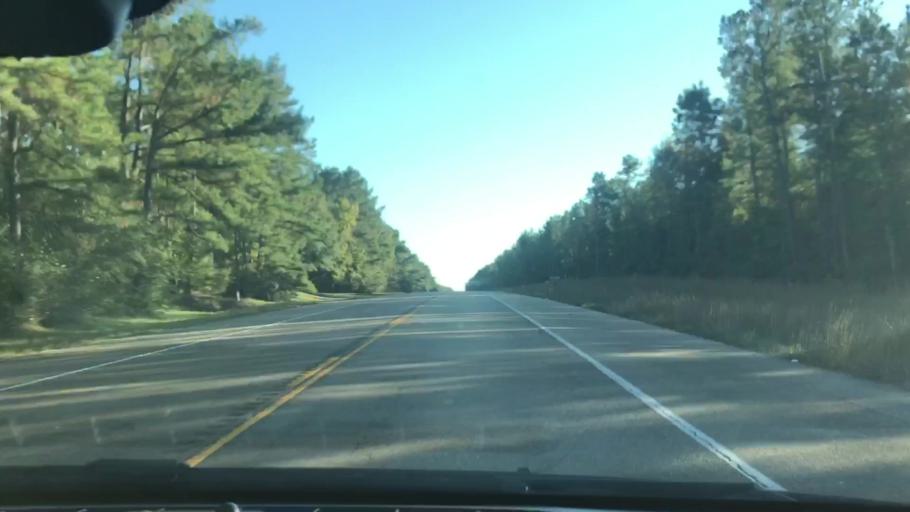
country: US
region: Louisiana
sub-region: Saint Tammany Parish
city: Abita Springs
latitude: 30.5859
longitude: -89.8715
